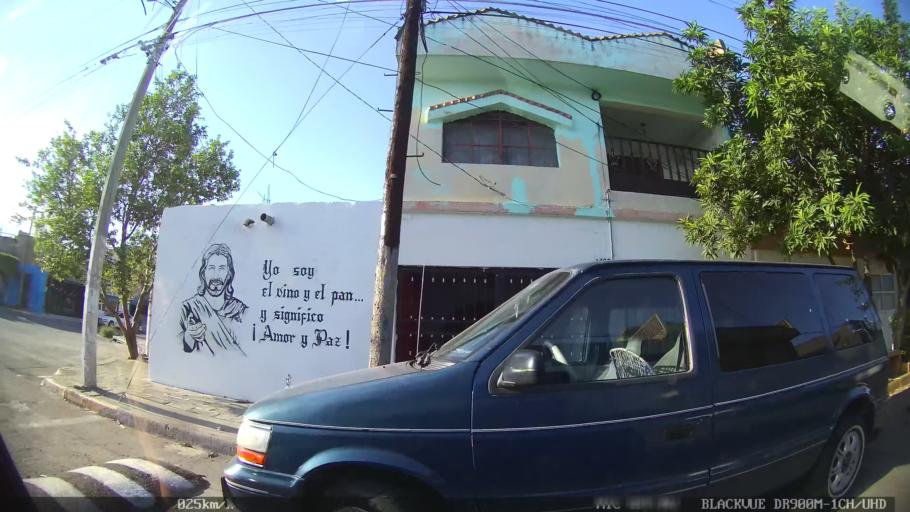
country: MX
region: Jalisco
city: Tlaquepaque
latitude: 20.6991
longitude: -103.3003
